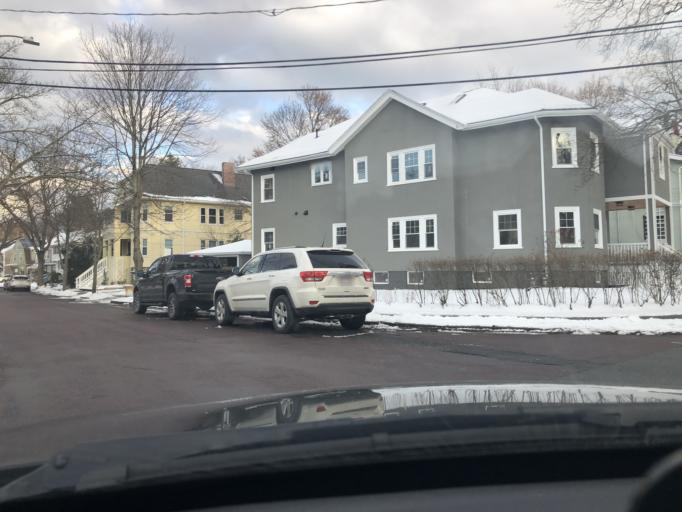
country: US
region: Massachusetts
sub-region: Middlesex County
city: Arlington
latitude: 42.4154
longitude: -71.1619
